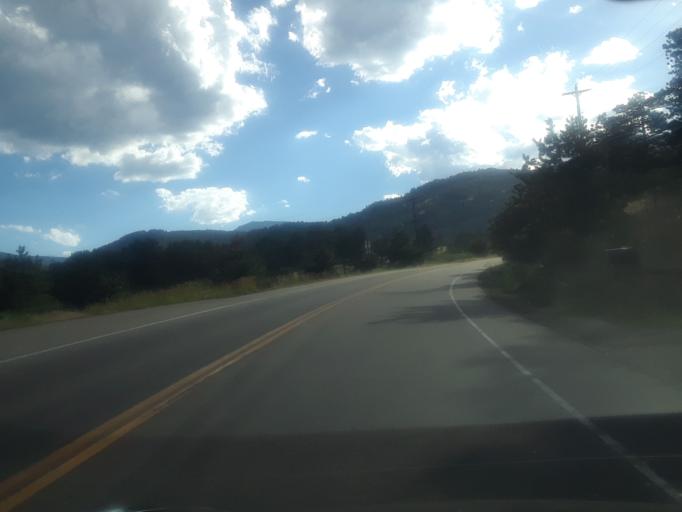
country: US
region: Colorado
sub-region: Jefferson County
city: Kittredge
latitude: 39.7162
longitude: -105.3920
